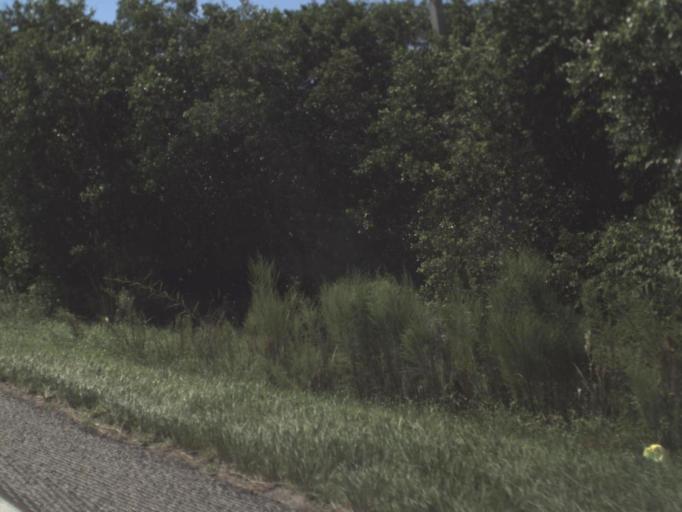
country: US
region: Florida
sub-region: Collier County
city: Marco
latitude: 26.0177
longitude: -81.7013
